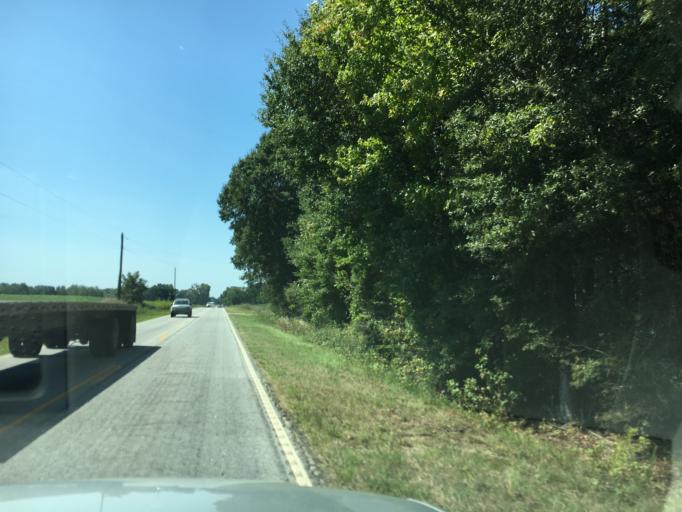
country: US
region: South Carolina
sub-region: Laurens County
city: Joanna
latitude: 34.3935
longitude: -81.8527
